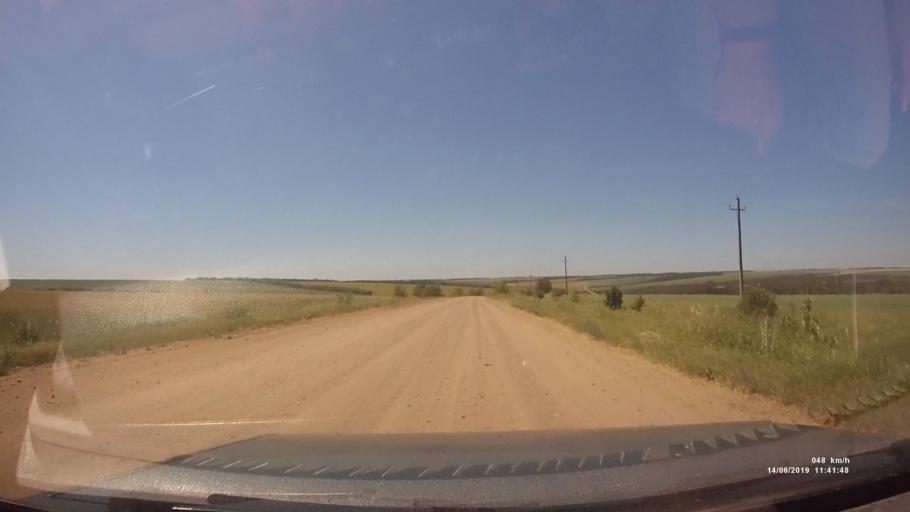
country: RU
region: Rostov
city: Kazanskaya
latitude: 49.8617
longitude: 41.3492
